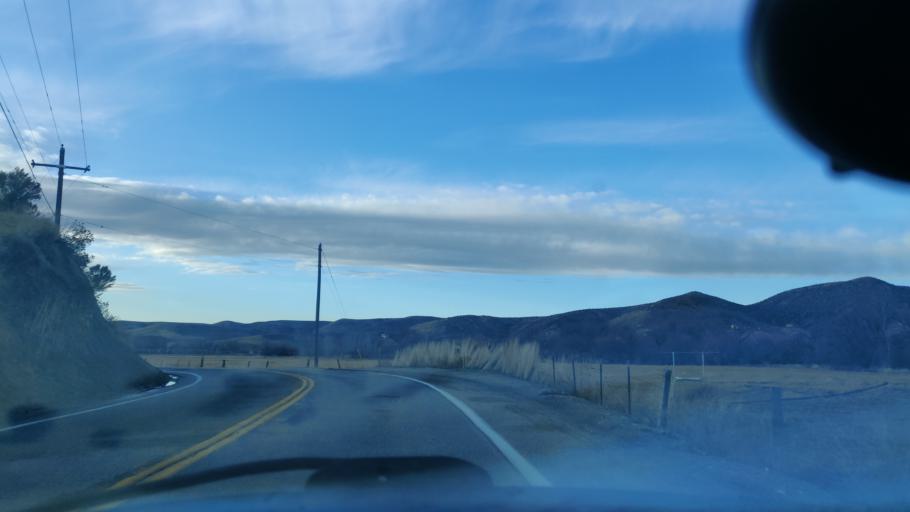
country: US
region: Idaho
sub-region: Ada County
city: Eagle
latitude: 43.7304
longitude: -116.2965
